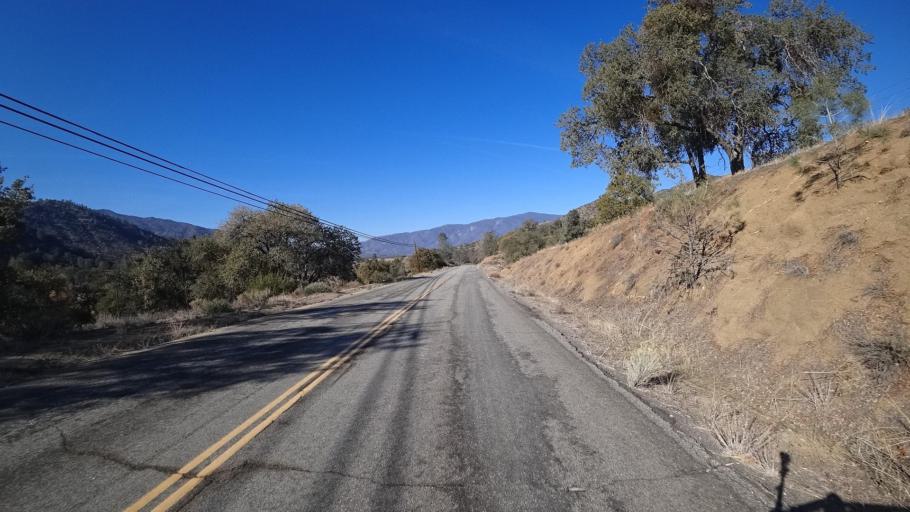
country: US
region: California
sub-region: Kern County
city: Bodfish
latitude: 35.3971
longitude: -118.4505
